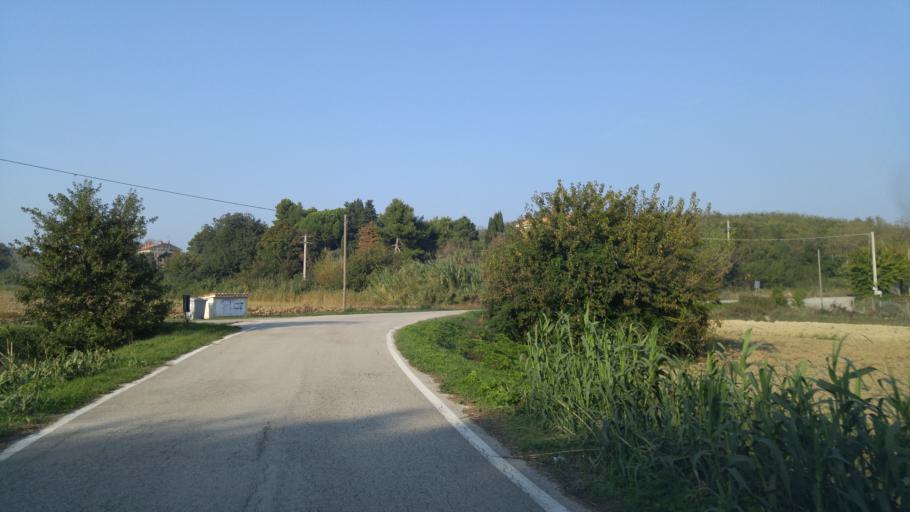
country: IT
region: The Marches
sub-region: Provincia di Pesaro e Urbino
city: Fenile
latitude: 43.8799
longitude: 12.9586
